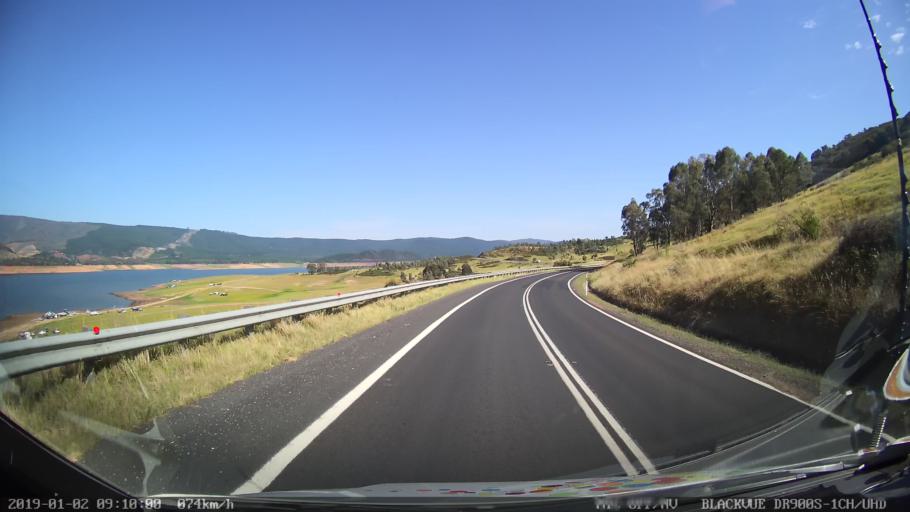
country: AU
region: New South Wales
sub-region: Tumut Shire
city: Tumut
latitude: -35.5257
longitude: 148.2727
